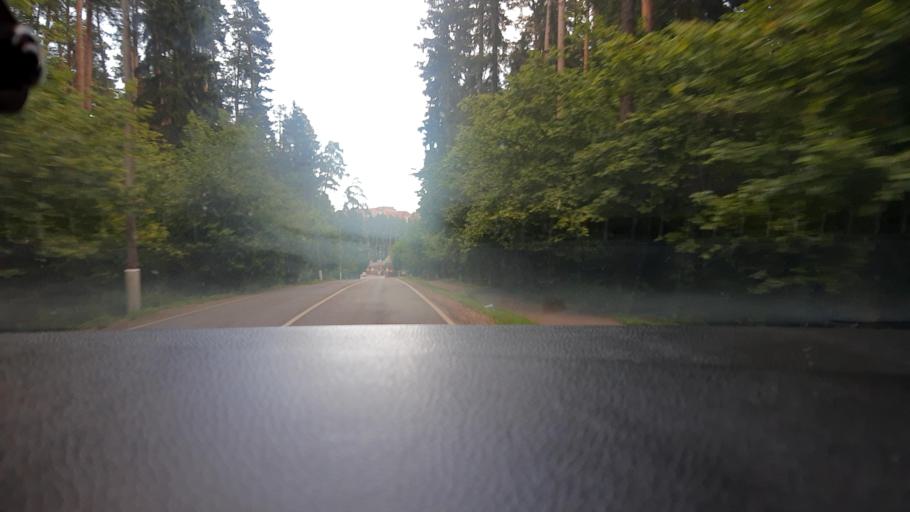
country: RU
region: Moskovskaya
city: Lesnoy Gorodok
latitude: 55.6767
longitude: 37.1847
